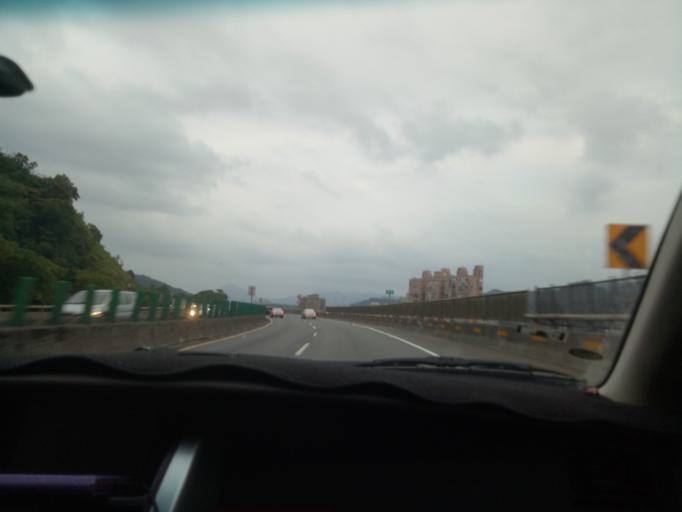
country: TW
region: Taiwan
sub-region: Keelung
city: Keelung
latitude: 25.1007
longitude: 121.7494
